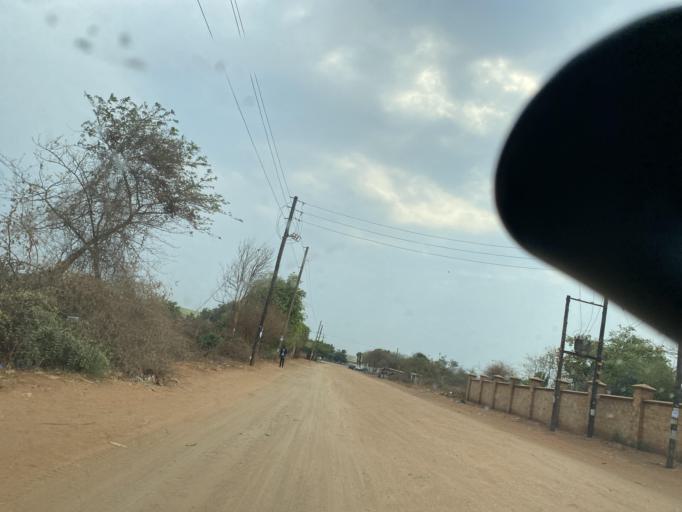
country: ZM
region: Lusaka
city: Lusaka
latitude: -15.2919
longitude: 28.2731
